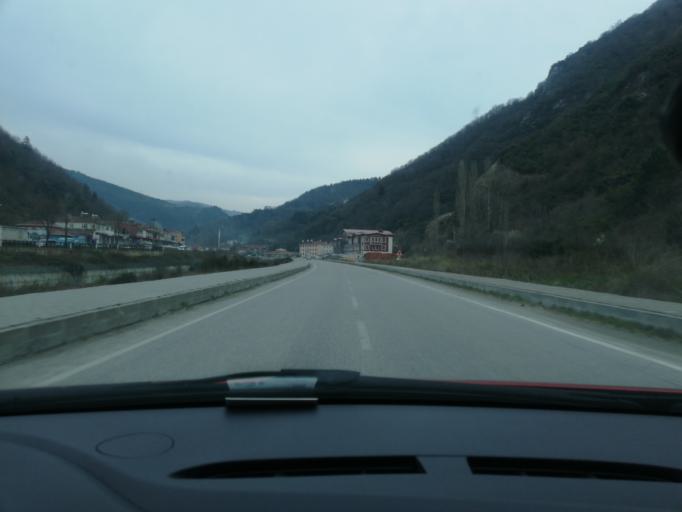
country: TR
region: Kastamonu
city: Inebolu
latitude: 41.9652
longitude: 33.7514
